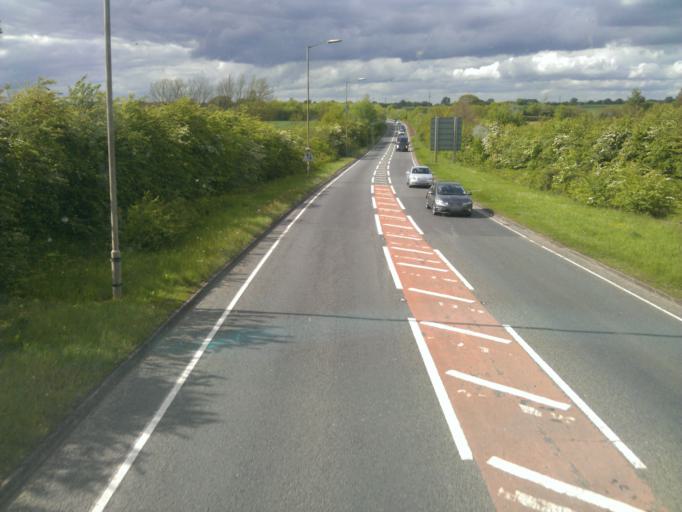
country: GB
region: England
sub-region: Essex
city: Coggeshall
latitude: 51.8745
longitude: 0.7009
